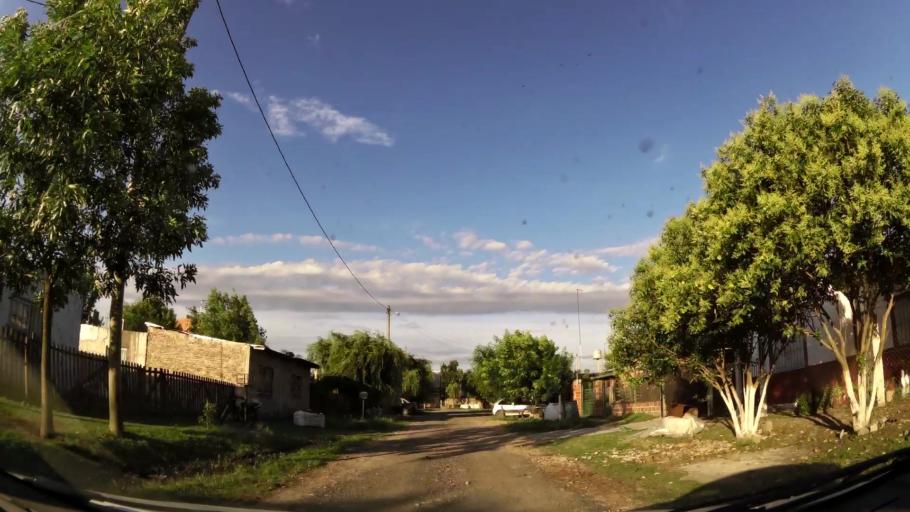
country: AR
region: Buenos Aires
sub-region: Partido de Merlo
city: Merlo
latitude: -34.6996
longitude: -58.7526
